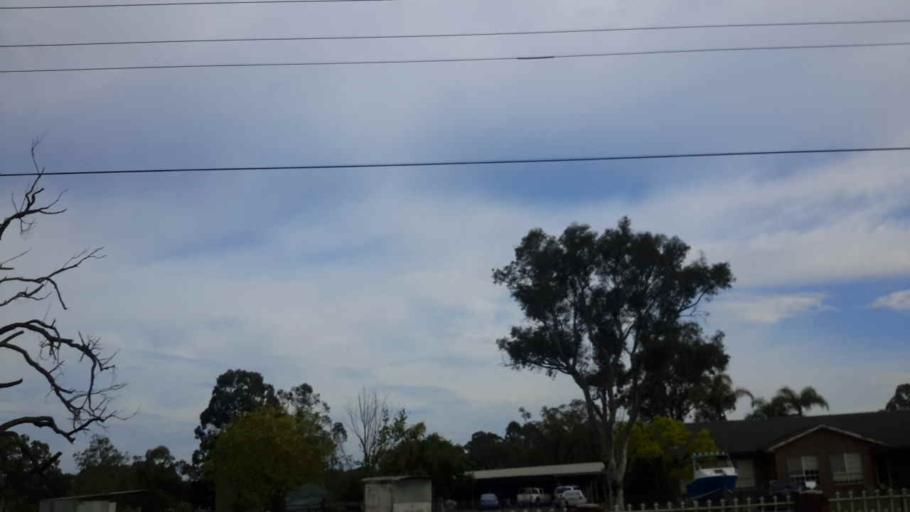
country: AU
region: New South Wales
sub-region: Hawkesbury
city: South Windsor
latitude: -33.6582
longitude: 150.7666
